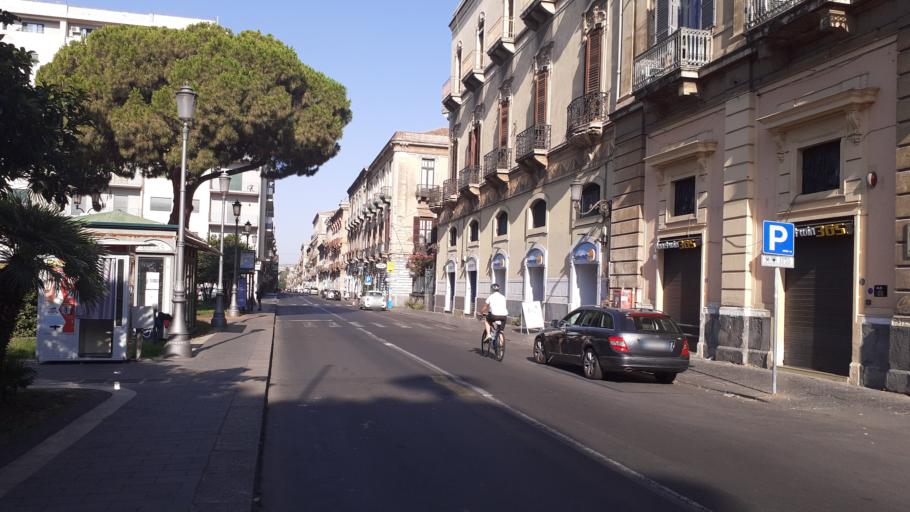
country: IT
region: Sicily
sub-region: Catania
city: Canalicchio
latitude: 37.5130
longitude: 15.0974
